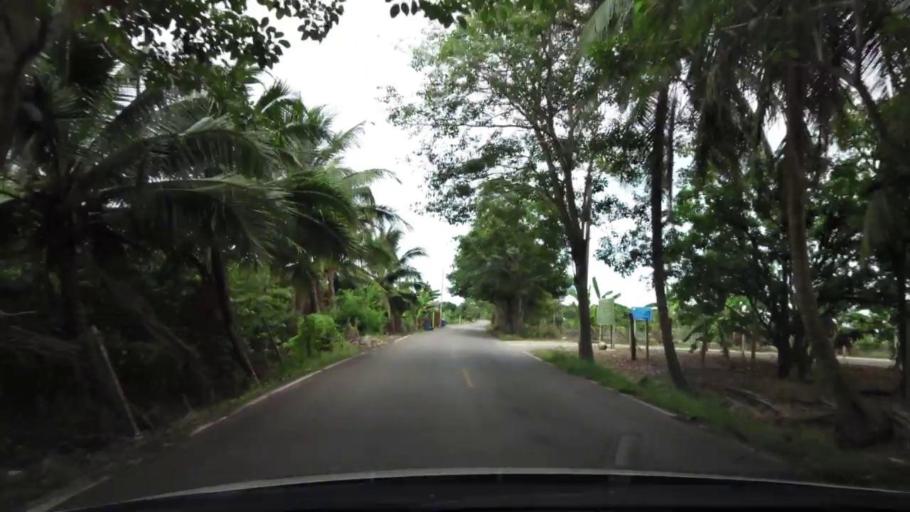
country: TH
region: Samut Sakhon
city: Ban Phaeo
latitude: 13.5688
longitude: 100.0317
